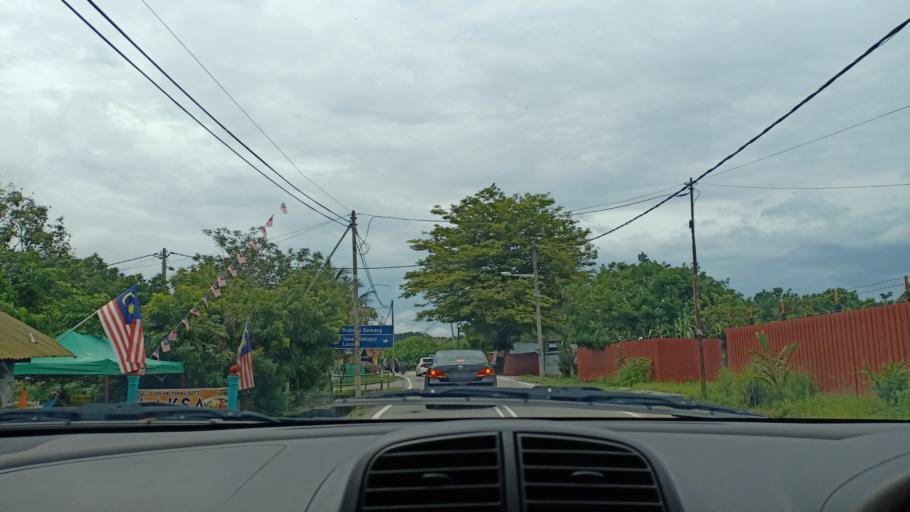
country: MY
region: Penang
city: Bukit Mertajam
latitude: 5.4080
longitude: 100.4837
